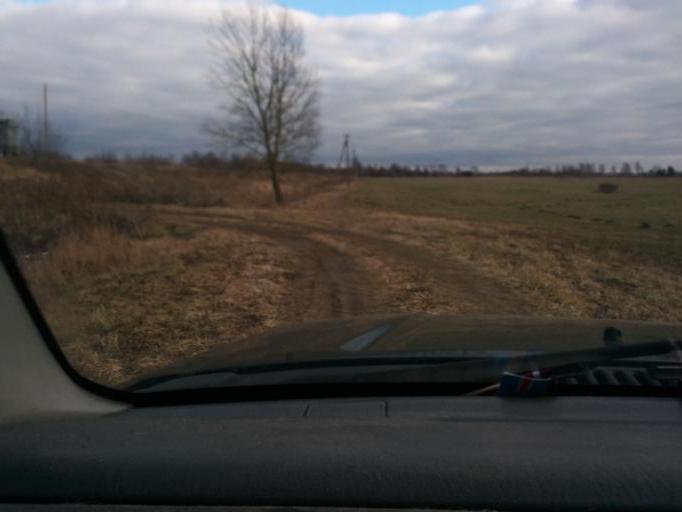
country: LV
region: Jelgava
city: Jelgava
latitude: 56.6879
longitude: 23.6918
